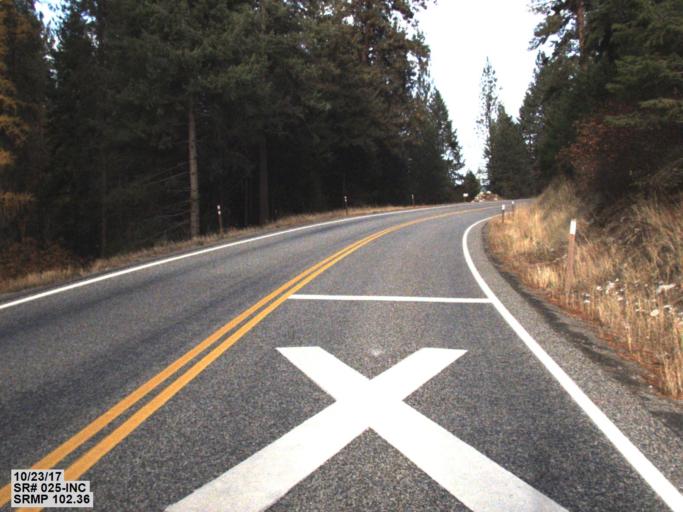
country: US
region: Washington
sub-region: Stevens County
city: Kettle Falls
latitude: 48.8129
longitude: -117.9372
